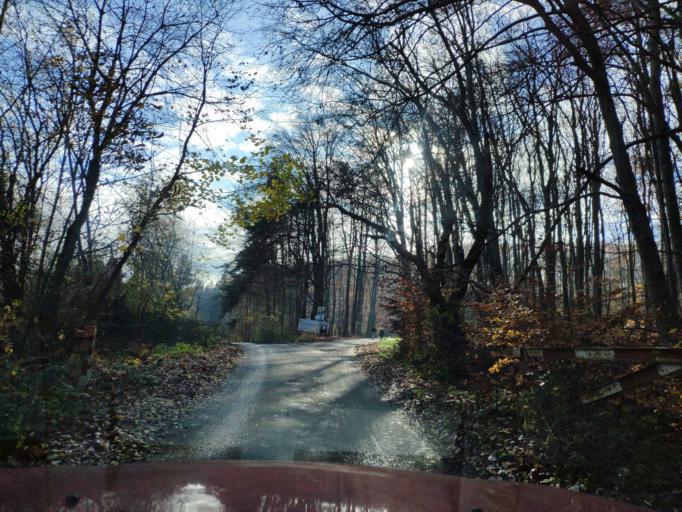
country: SK
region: Kosicky
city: Kosice
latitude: 48.6303
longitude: 21.4528
